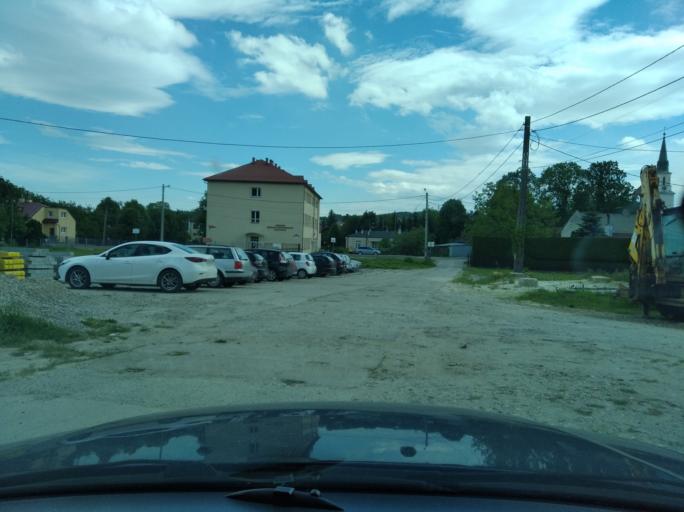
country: PL
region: Subcarpathian Voivodeship
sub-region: Powiat ropczycko-sedziszowski
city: Ropczyce
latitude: 50.0556
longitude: 21.6101
